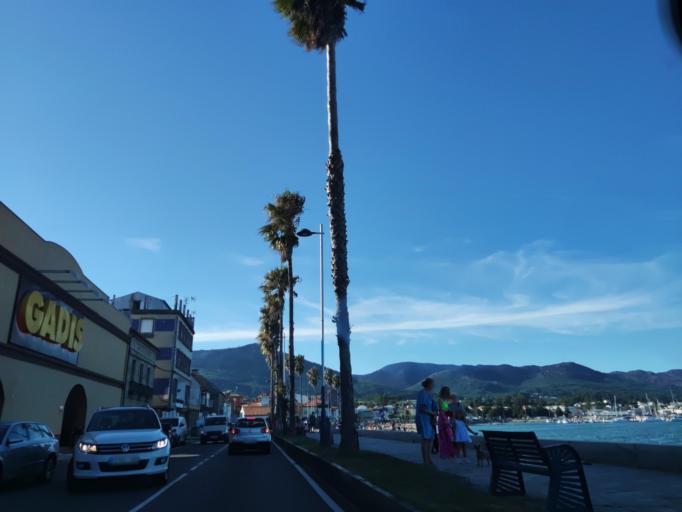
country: ES
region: Galicia
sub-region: Provincia da Coruna
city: Boiro
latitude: 42.6005
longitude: -8.9353
